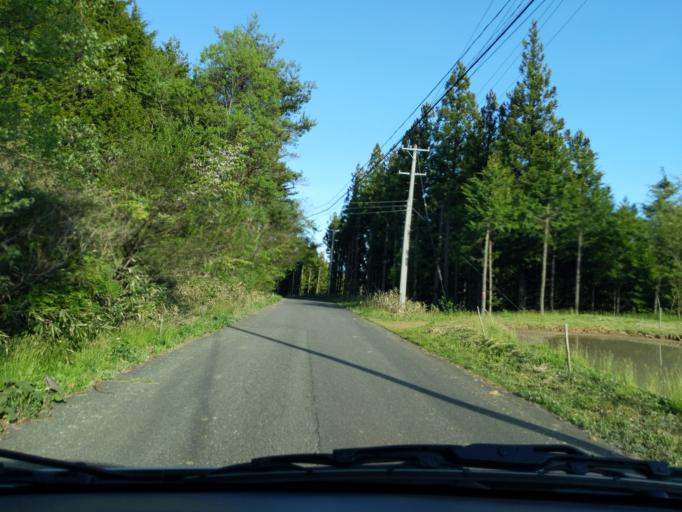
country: JP
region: Iwate
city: Ichinoseki
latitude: 38.8747
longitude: 140.9318
